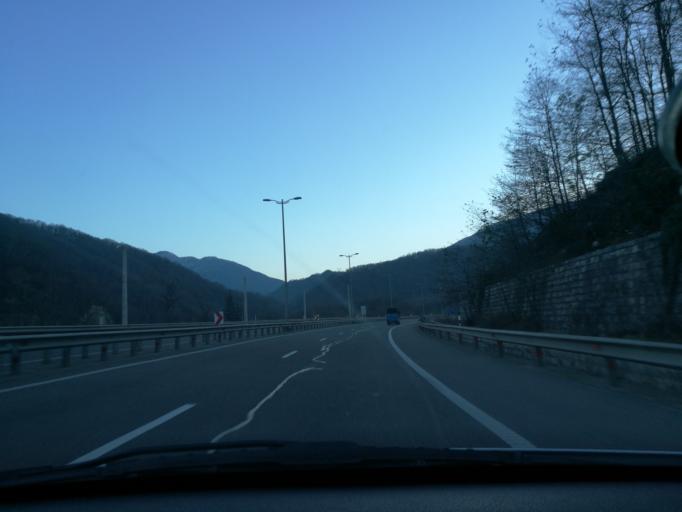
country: IR
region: Mazandaran
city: Chalus
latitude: 36.6118
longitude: 51.3868
